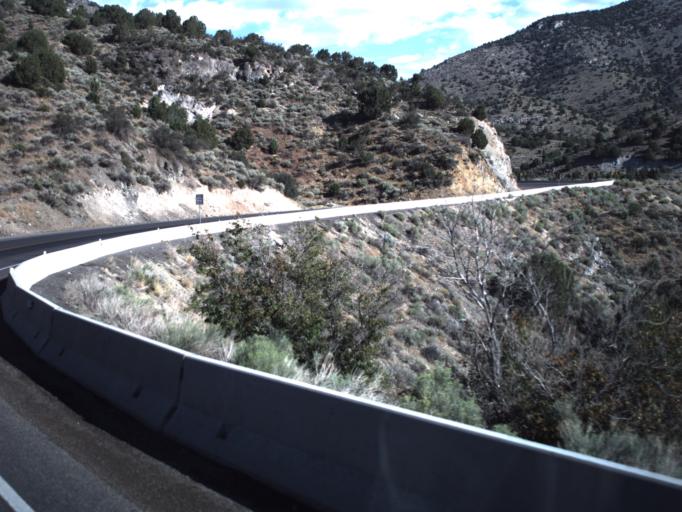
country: US
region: Utah
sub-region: Utah County
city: Genola
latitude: 39.9728
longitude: -112.0677
